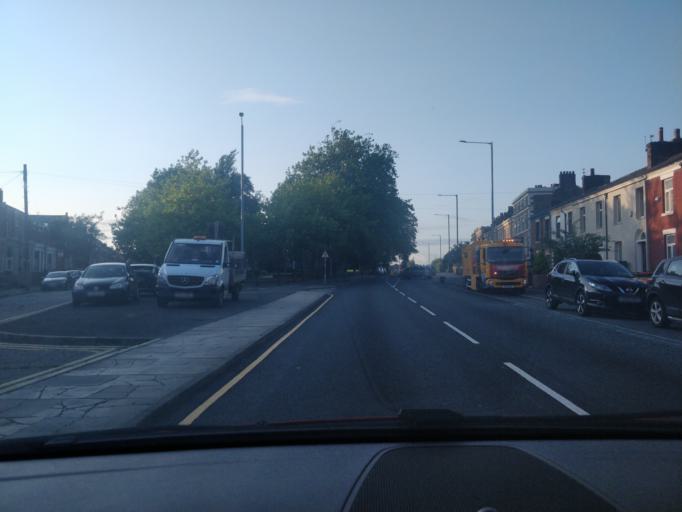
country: GB
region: England
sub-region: Lancashire
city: Preston
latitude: 53.7631
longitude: -2.6905
